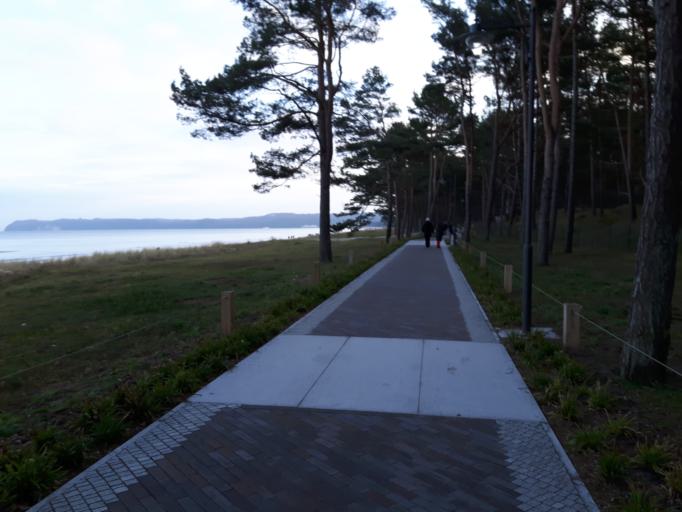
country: DE
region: Mecklenburg-Vorpommern
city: Ostseebad Binz
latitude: 54.4201
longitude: 13.5915
